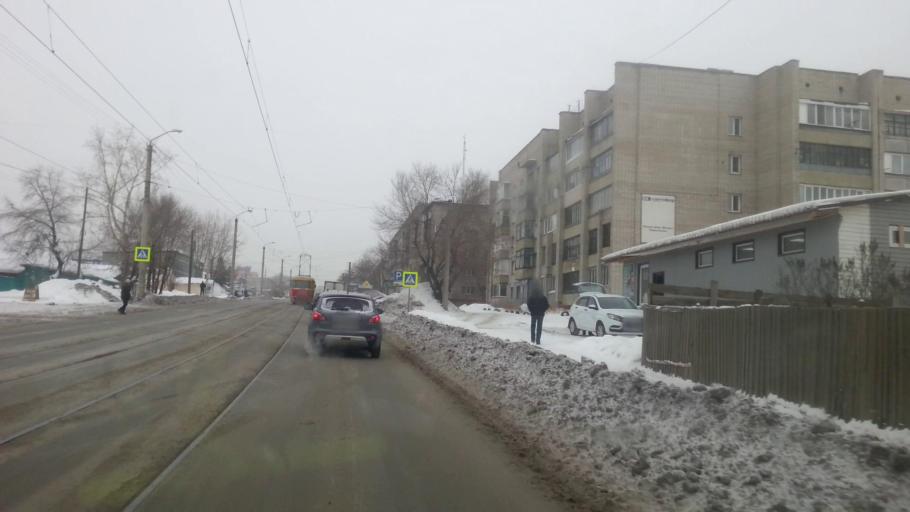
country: RU
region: Altai Krai
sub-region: Gorod Barnaulskiy
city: Barnaul
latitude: 53.3331
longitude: 83.7570
